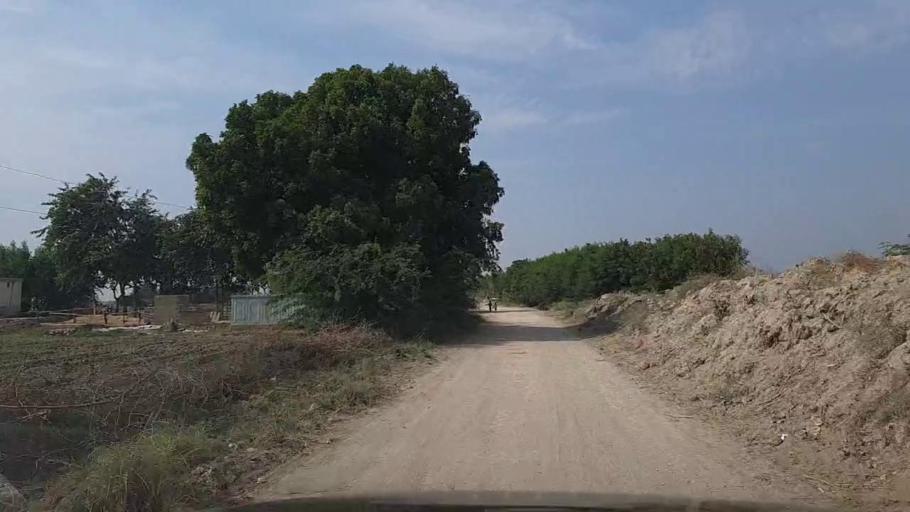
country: PK
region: Sindh
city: Thatta
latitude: 24.7991
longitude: 67.8809
